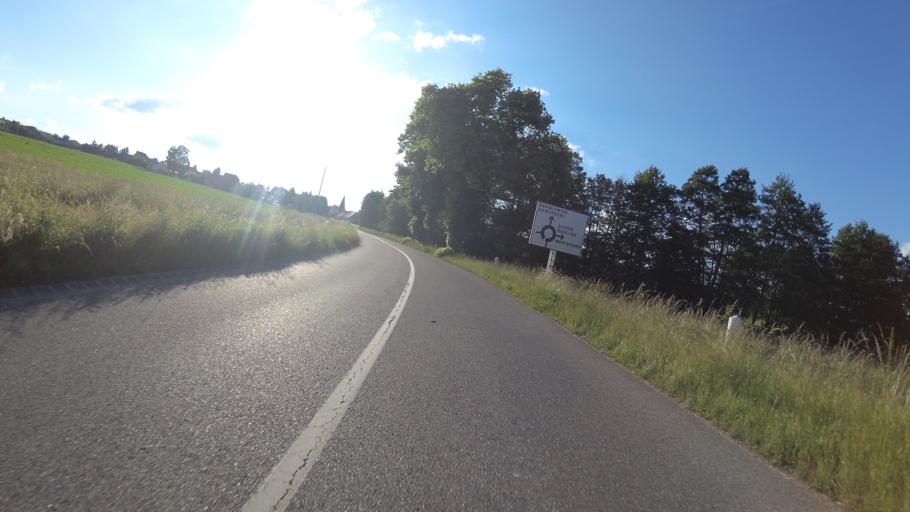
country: FR
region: Alsace
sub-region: Departement du Bas-Rhin
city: Diemeringen
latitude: 48.9507
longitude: 7.1823
